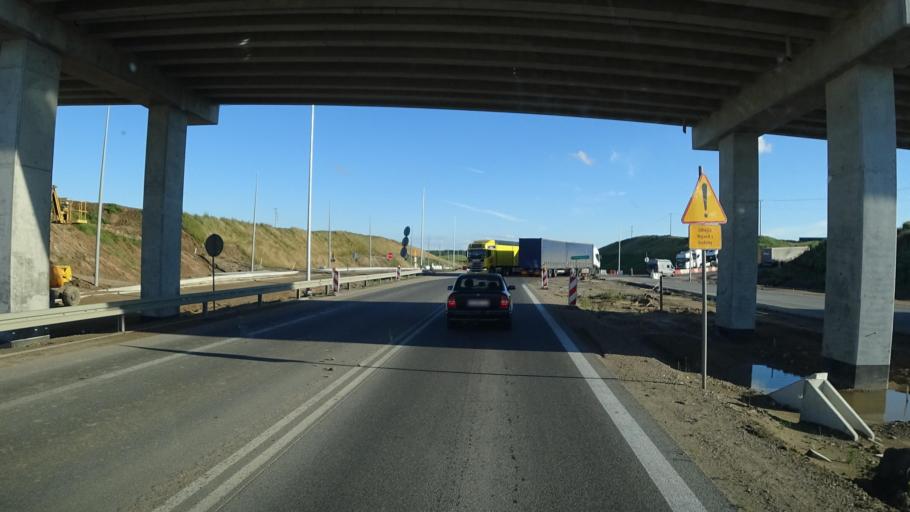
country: PL
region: Podlasie
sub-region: Powiat sejnenski
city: Punsk
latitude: 54.2971
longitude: 23.1164
